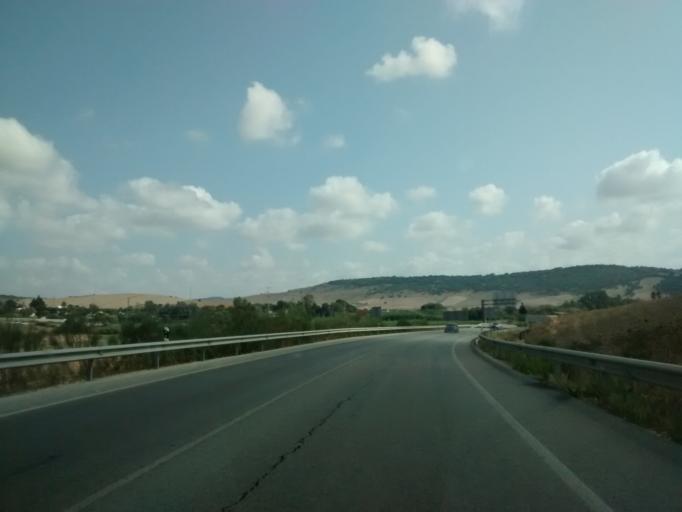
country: ES
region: Andalusia
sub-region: Provincia de Cadiz
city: Vejer de la Frontera
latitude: 36.2593
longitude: -5.9752
